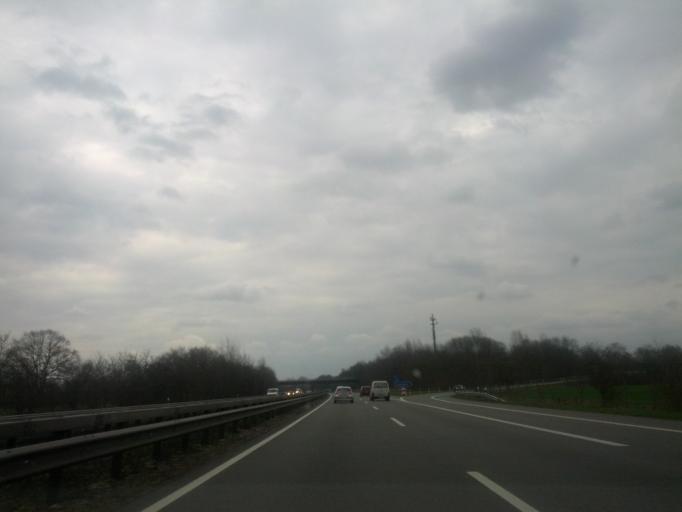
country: DE
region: Lower Saxony
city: Hatten
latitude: 53.0638
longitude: 8.3486
